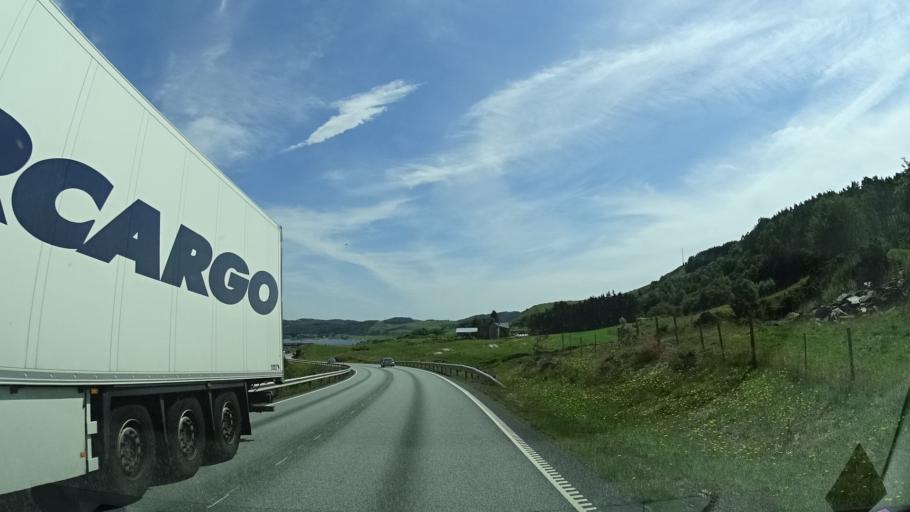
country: NO
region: Rogaland
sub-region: Rennesoy
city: Vikevag
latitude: 59.1255
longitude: 5.6640
